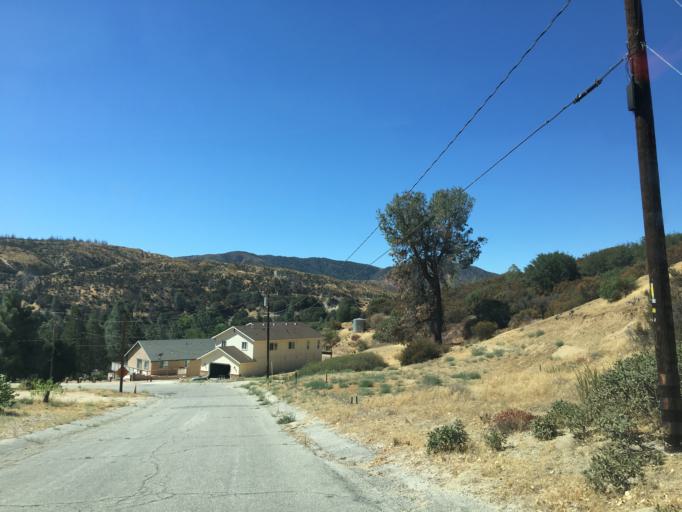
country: US
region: California
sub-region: Los Angeles County
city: Green Valley
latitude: 34.6794
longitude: -118.4479
